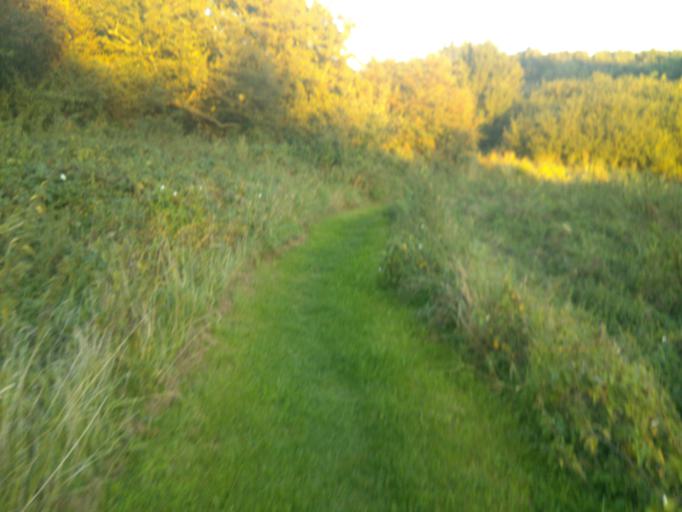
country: DK
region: South Denmark
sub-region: Fredericia Kommune
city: Fredericia
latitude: 55.5731
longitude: 9.7049
